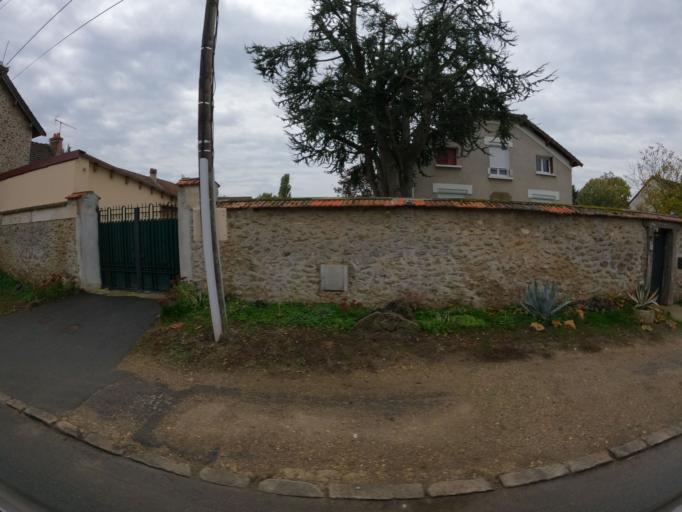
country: FR
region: Ile-de-France
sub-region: Departement de Seine-et-Marne
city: Chanteloup-en-Brie
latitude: 48.8353
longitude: 2.7531
